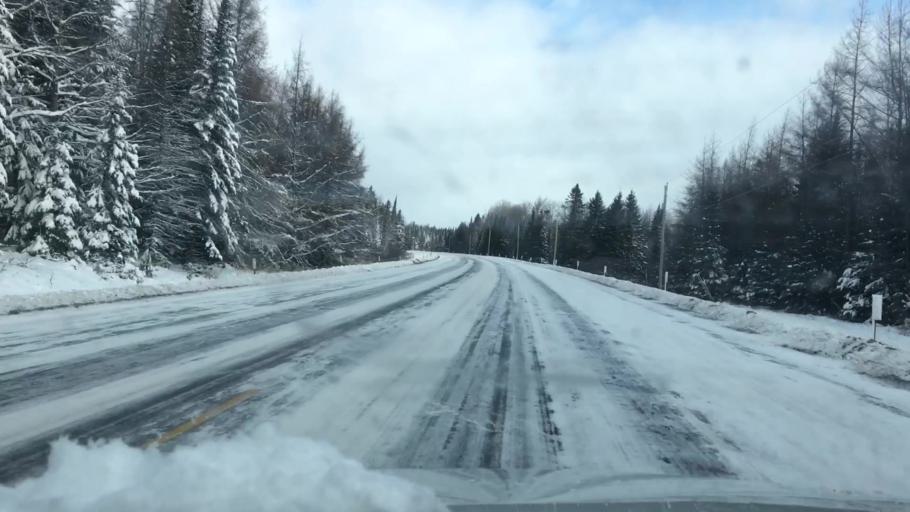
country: US
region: Maine
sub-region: Aroostook County
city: Van Buren
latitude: 47.0673
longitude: -67.9874
